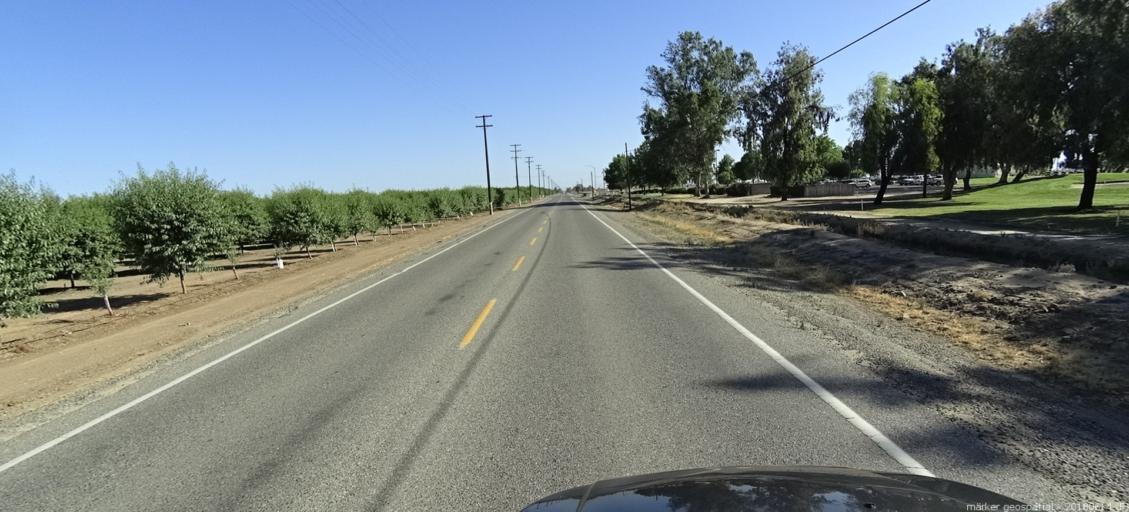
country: US
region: California
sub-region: Madera County
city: Madera Acres
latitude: 36.9938
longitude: -120.1286
